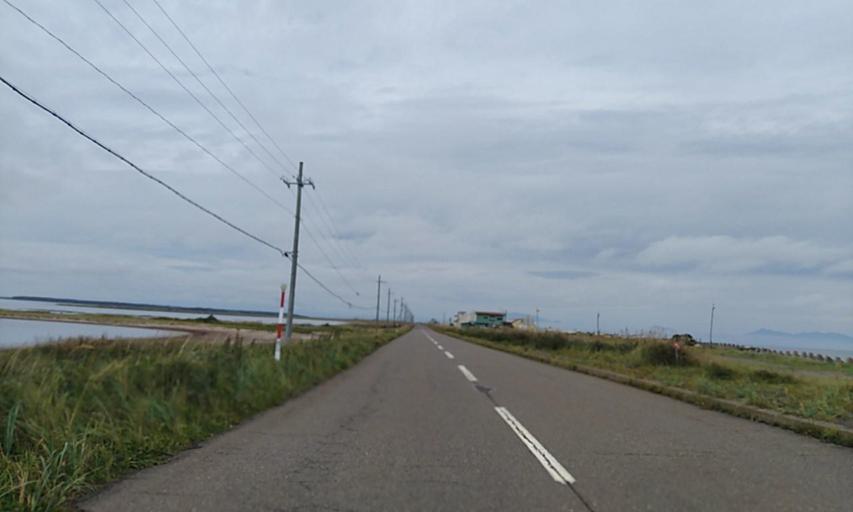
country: JP
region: Hokkaido
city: Shibetsu
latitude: 43.5920
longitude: 145.3331
